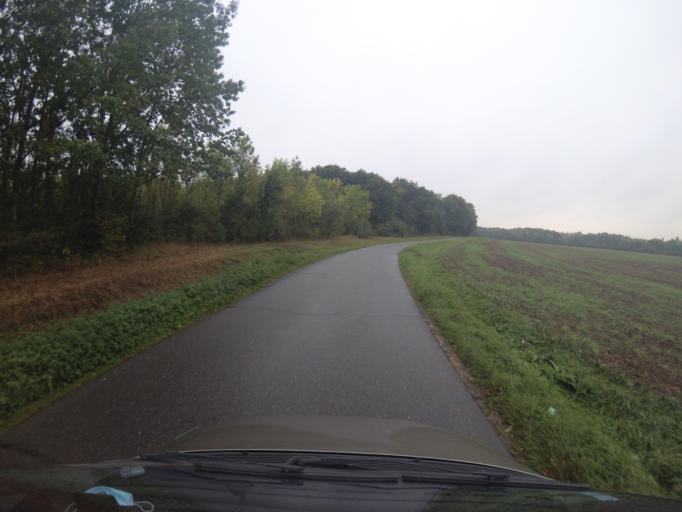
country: FR
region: Ile-de-France
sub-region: Departement de Seine-et-Marne
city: Ferrieres-en-Brie
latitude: 48.8257
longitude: 2.6903
